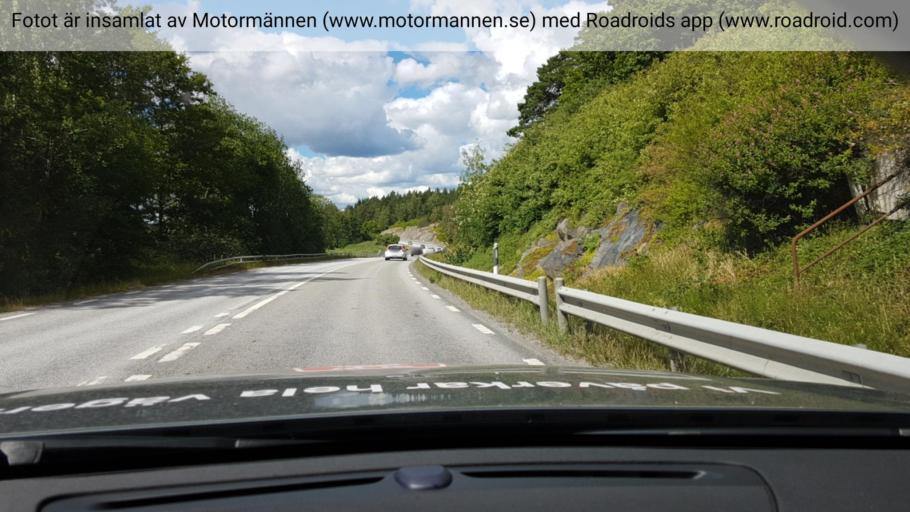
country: SE
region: Stockholm
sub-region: Vaxholms Kommun
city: Resaro
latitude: 59.4191
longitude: 18.3023
